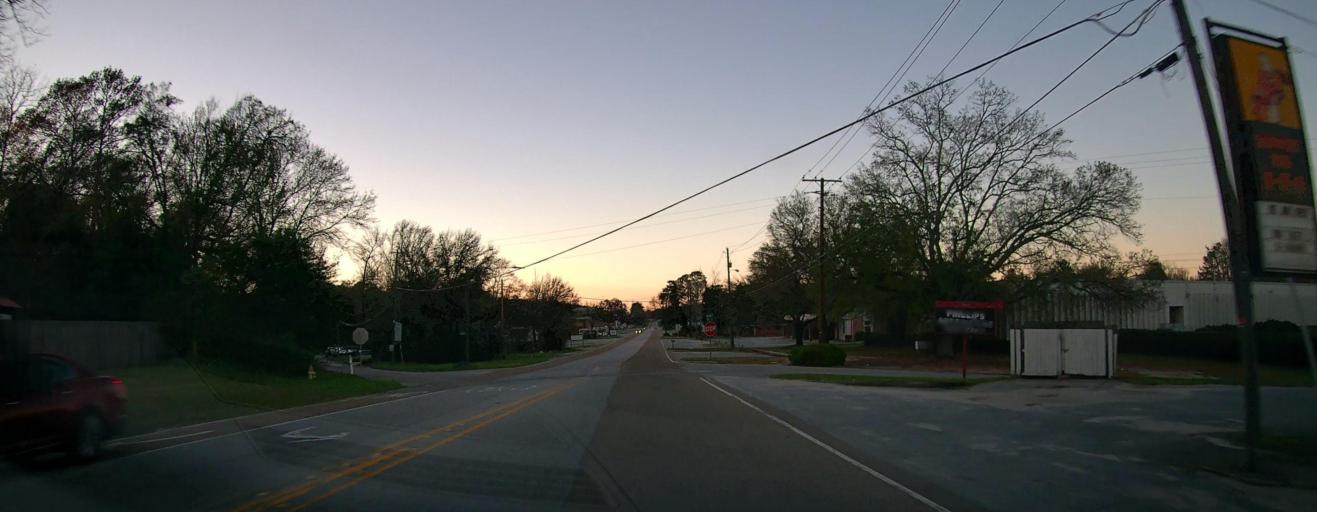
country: US
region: Alabama
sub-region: Russell County
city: Phenix City
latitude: 32.4753
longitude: -85.0244
